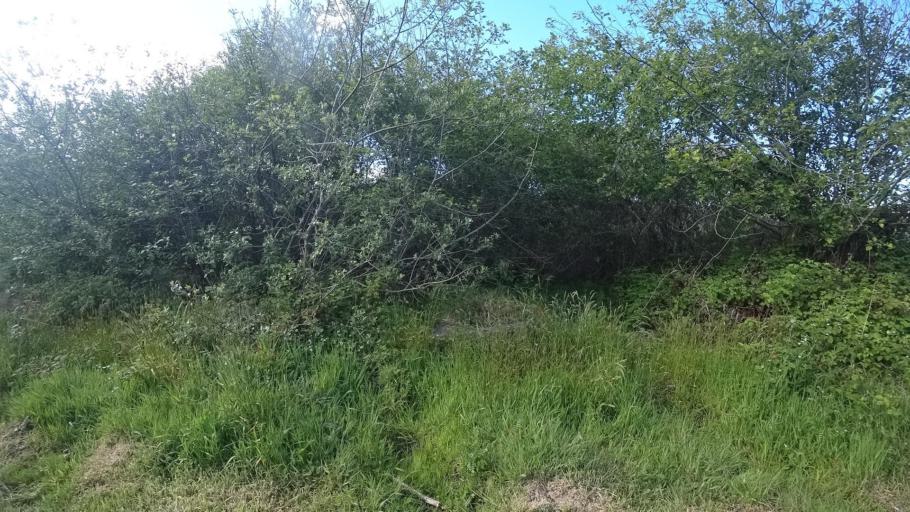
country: US
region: California
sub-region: Humboldt County
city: McKinleyville
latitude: 40.9941
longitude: -124.1147
